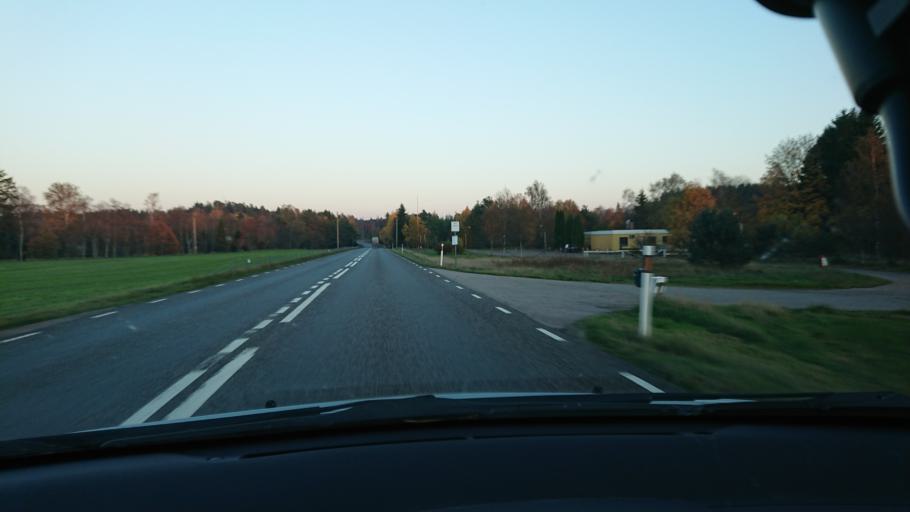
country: SE
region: Halland
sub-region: Laholms Kommun
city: Knared
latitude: 56.7134
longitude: 13.2507
